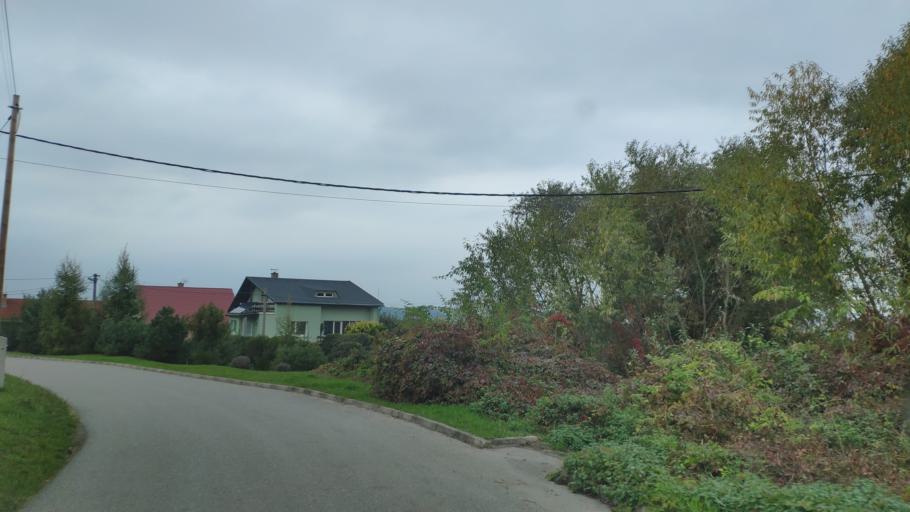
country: SK
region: Kosicky
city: Kosice
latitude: 48.6347
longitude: 21.3932
